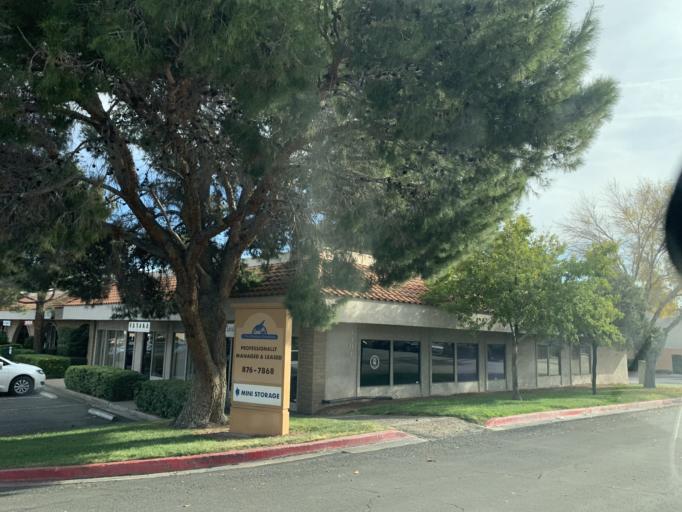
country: US
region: Nevada
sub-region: Clark County
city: Paradise
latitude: 36.1260
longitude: -115.1833
